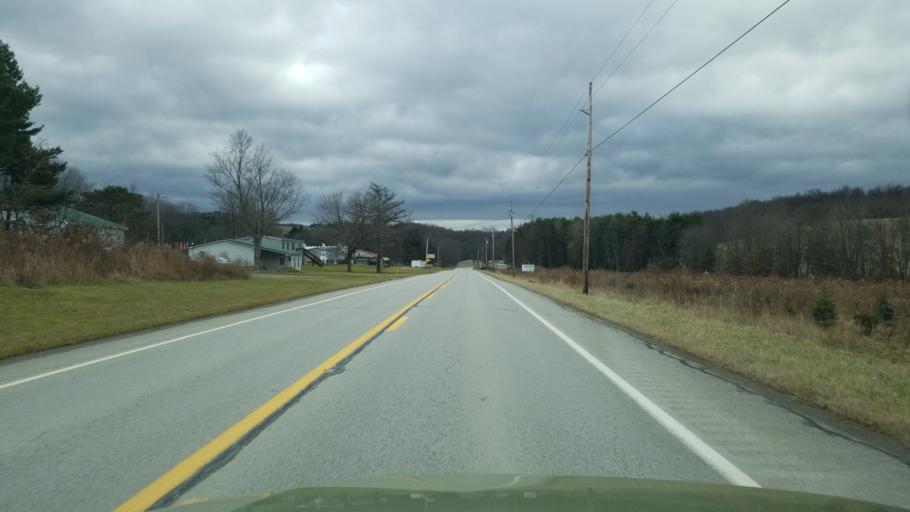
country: US
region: Pennsylvania
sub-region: Indiana County
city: Clymer
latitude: 40.7875
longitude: -79.0542
